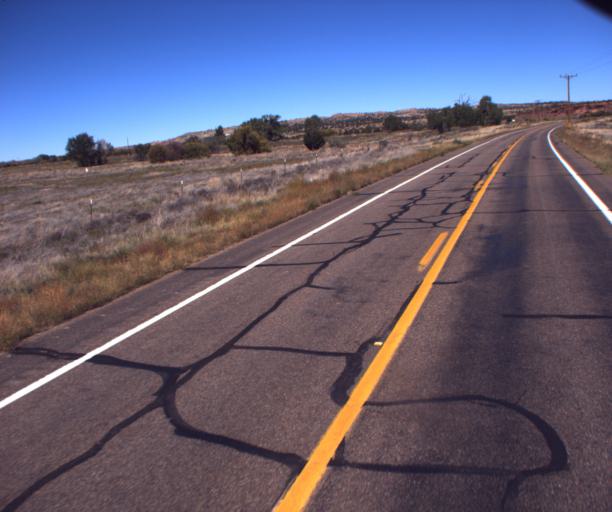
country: US
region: Arizona
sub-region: Apache County
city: Saint Johns
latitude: 34.4439
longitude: -109.4106
